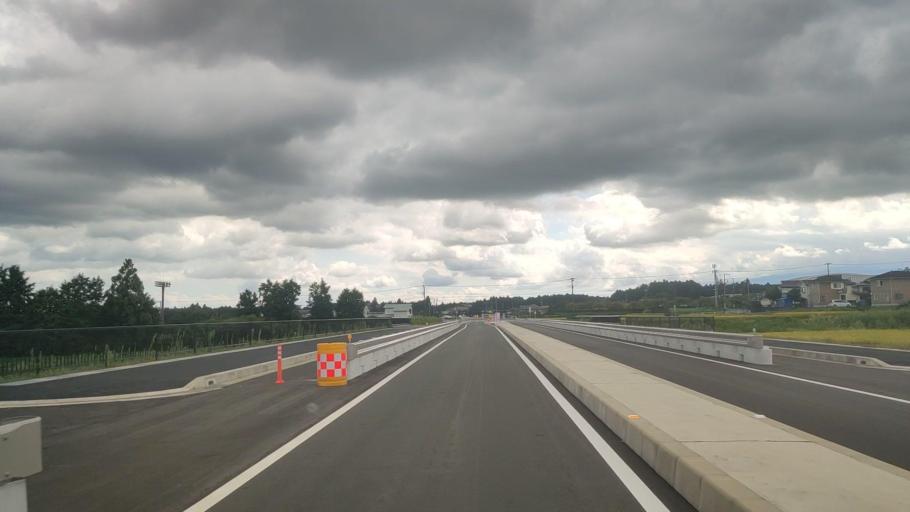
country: JP
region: Shizuoka
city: Gotemba
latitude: 35.3170
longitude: 138.9101
